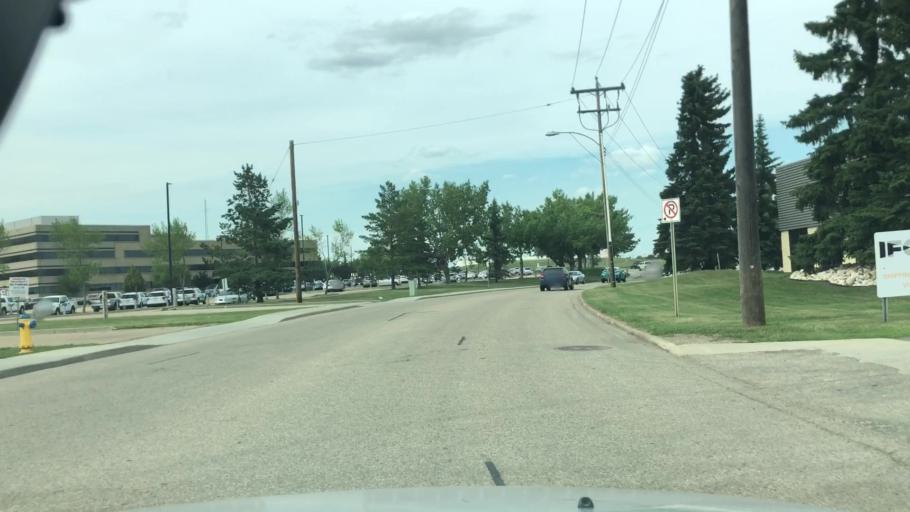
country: CA
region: Alberta
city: Edmonton
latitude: 53.5347
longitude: -113.4149
